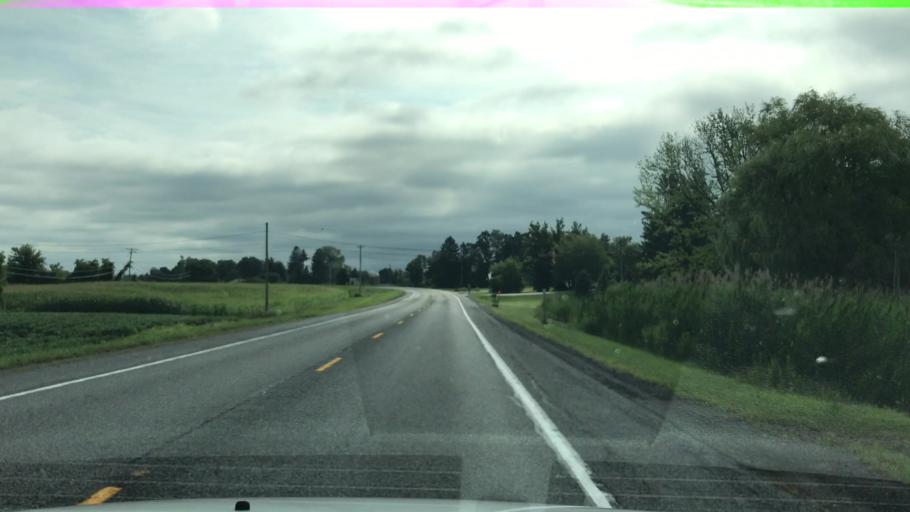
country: US
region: New York
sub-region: Erie County
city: Alden
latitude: 42.8354
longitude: -78.4087
